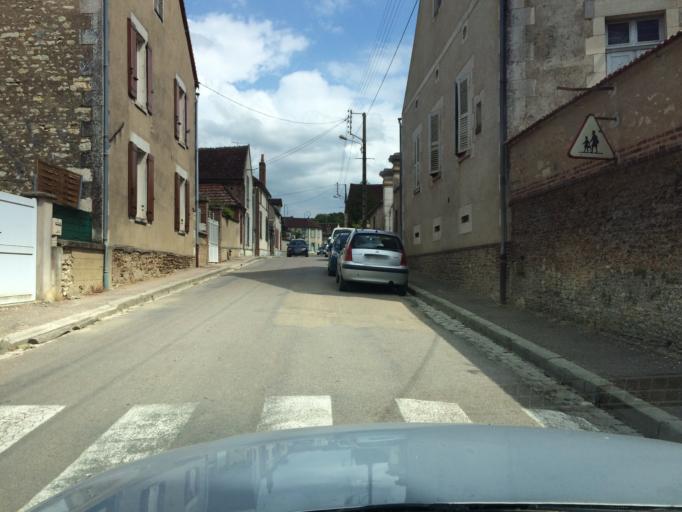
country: FR
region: Bourgogne
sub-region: Departement de l'Yonne
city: Fleury-la-Vallee
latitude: 47.8926
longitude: 3.4378
